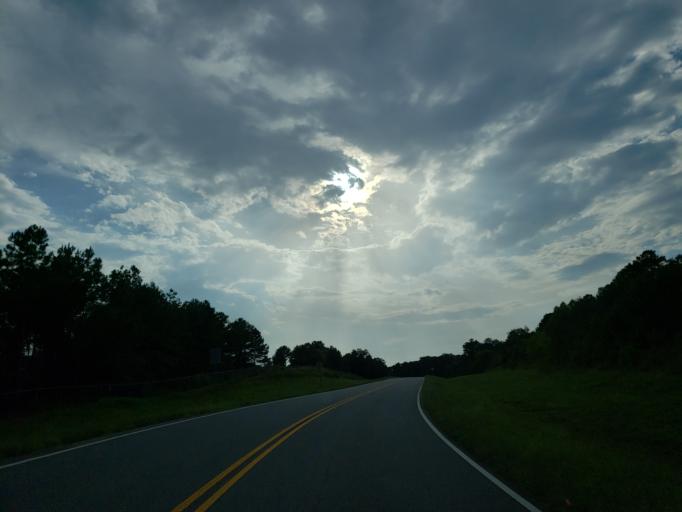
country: US
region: Georgia
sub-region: Bartow County
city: Euharlee
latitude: 34.1366
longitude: -84.9279
